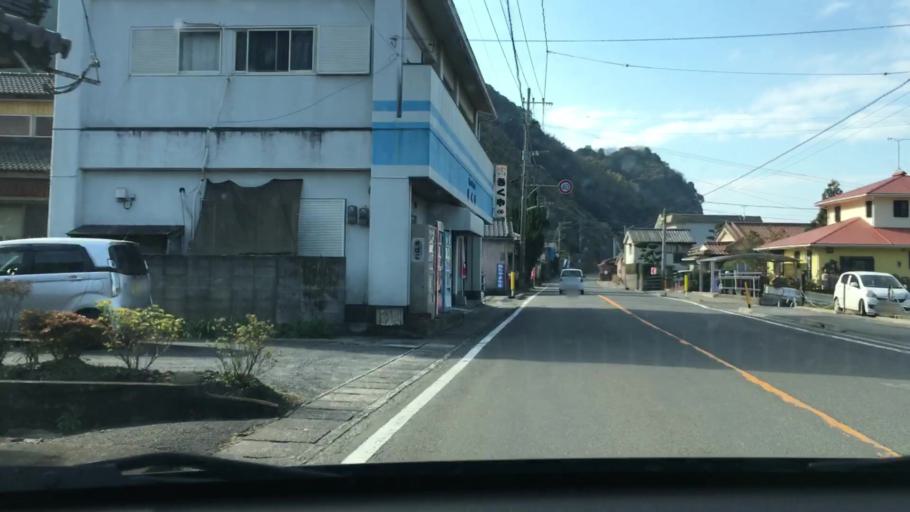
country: JP
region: Kagoshima
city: Hamanoichi
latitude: 31.6088
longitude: 130.7939
